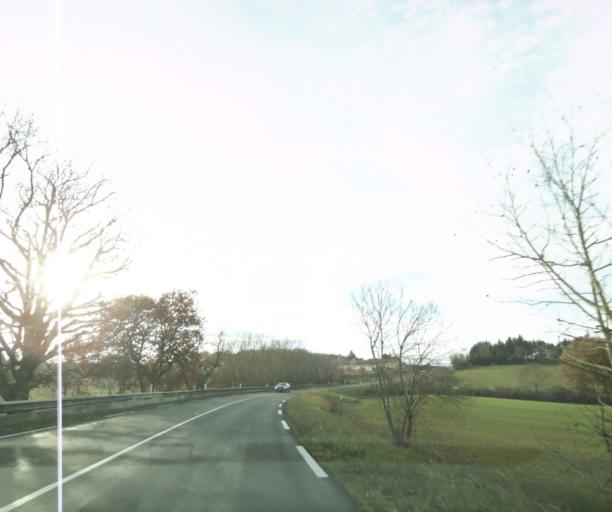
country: FR
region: Midi-Pyrenees
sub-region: Departement du Gers
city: Vic-Fezensac
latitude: 43.7498
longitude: 0.2797
